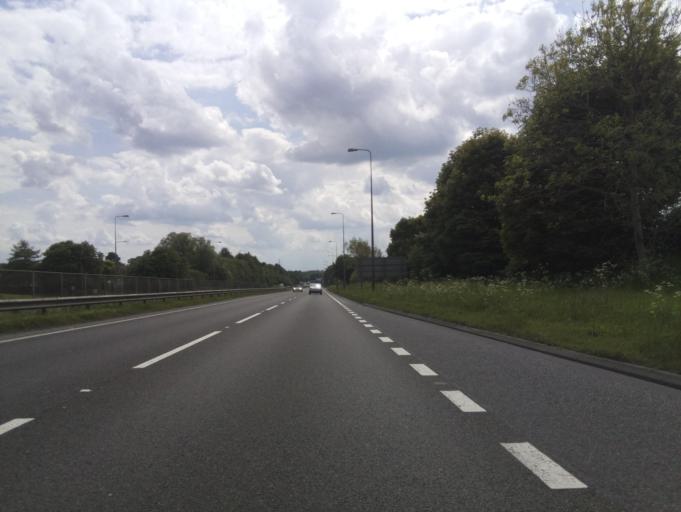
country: GB
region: England
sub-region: County Durham
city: Wingate
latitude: 54.7504
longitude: -1.3623
